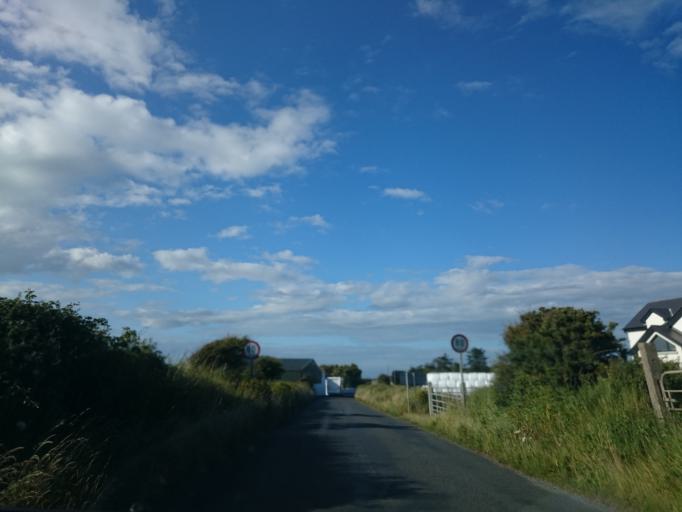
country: IE
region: Leinster
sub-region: Loch Garman
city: Loch Garman
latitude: 52.1798
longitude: -6.5833
